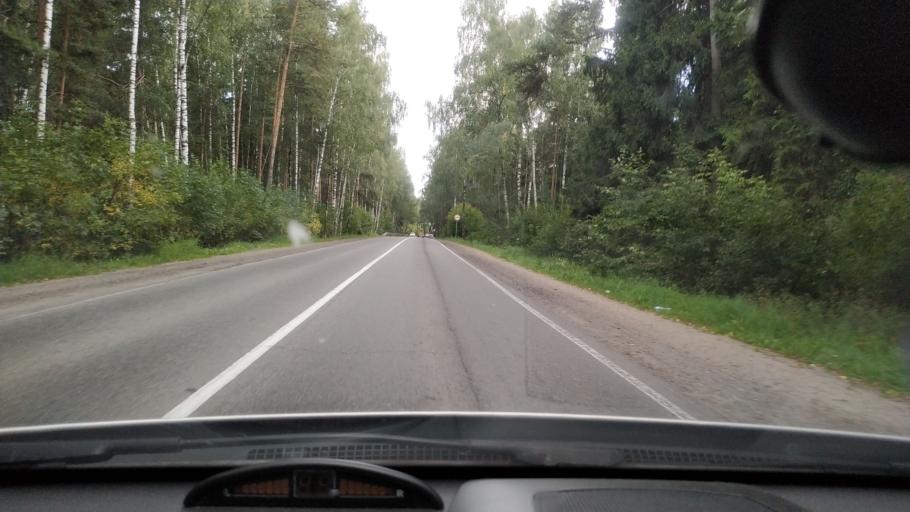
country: RU
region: Moskovskaya
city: Chornaya
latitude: 55.7800
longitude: 38.0424
